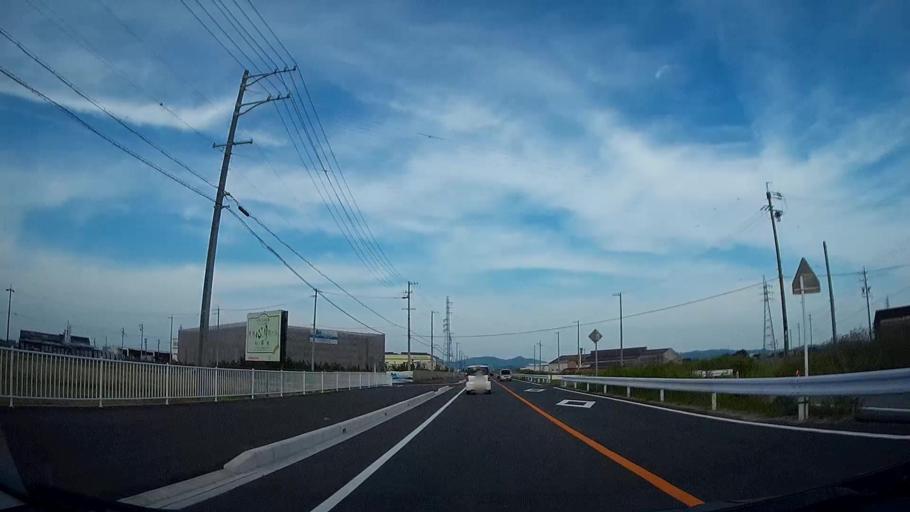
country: JP
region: Aichi
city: Nishio
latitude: 34.8482
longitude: 137.0308
